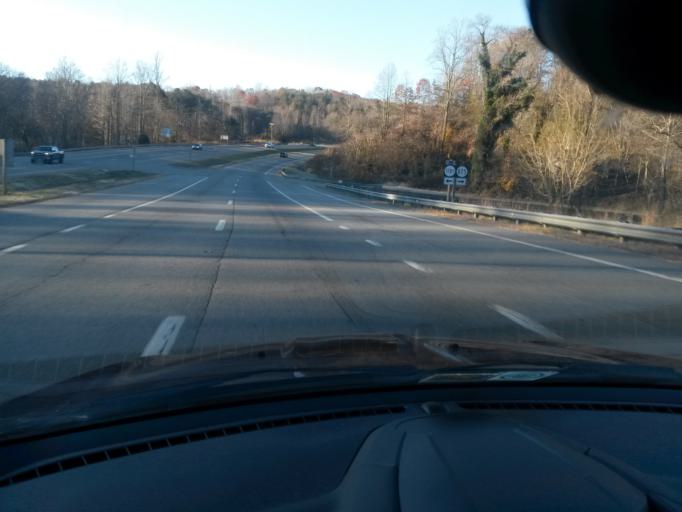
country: US
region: Virginia
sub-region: Henry County
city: Horse Pasture
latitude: 36.6450
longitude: -79.9194
